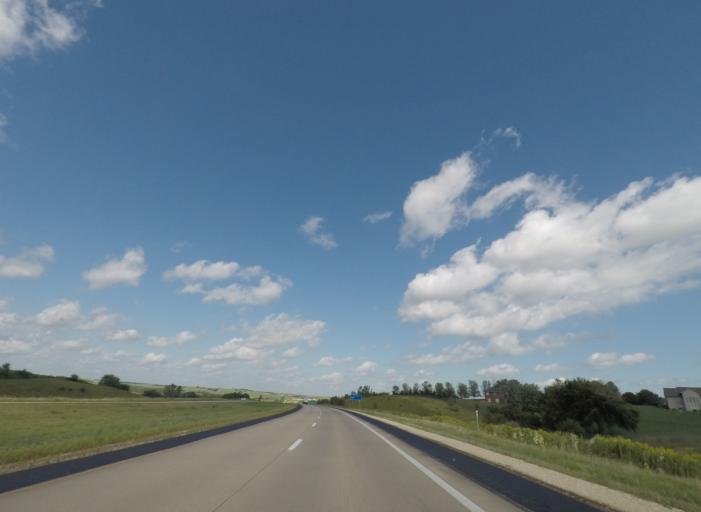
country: US
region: Iowa
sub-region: Dubuque County
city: Cascade
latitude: 42.2968
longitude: -91.0333
